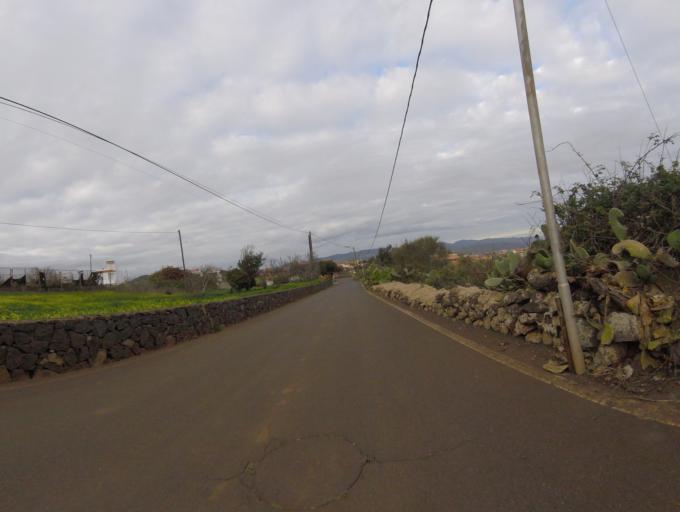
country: ES
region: Canary Islands
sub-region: Provincia de Santa Cruz de Tenerife
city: La Laguna
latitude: 28.4440
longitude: -16.3362
